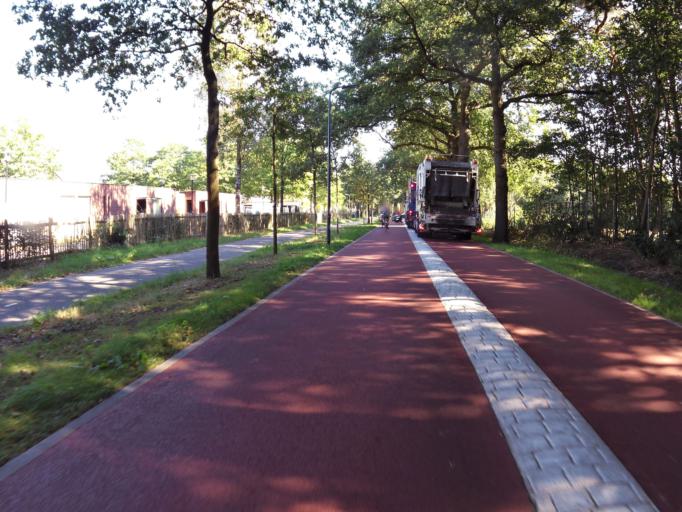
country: NL
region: North Brabant
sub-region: Gemeente Maasdonk
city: Geffen
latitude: 51.7207
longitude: 5.4033
